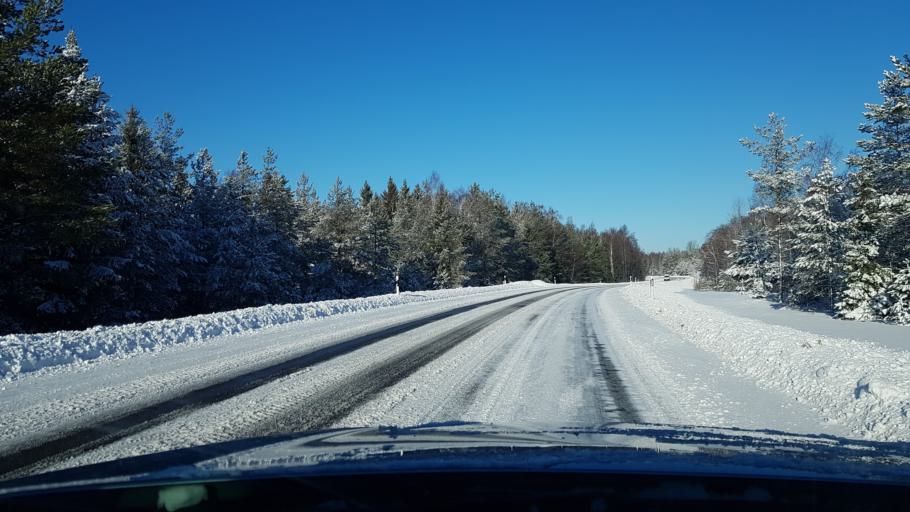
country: EE
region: Hiiumaa
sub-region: Kaerdla linn
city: Kardla
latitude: 58.9625
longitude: 22.7719
